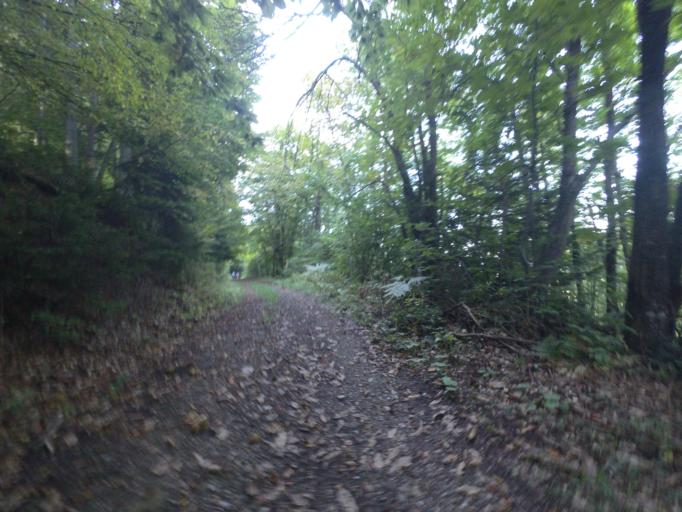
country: AT
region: Styria
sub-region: Politischer Bezirk Leibnitz
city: Kitzeck im Sausal
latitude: 46.7837
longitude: 15.4319
